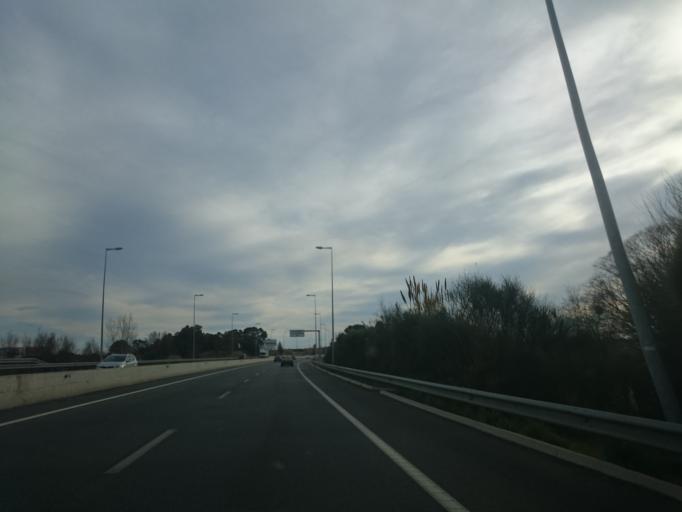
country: ES
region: Catalonia
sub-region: Provincia de Barcelona
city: Viladecans
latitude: 41.2847
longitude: 2.0526
